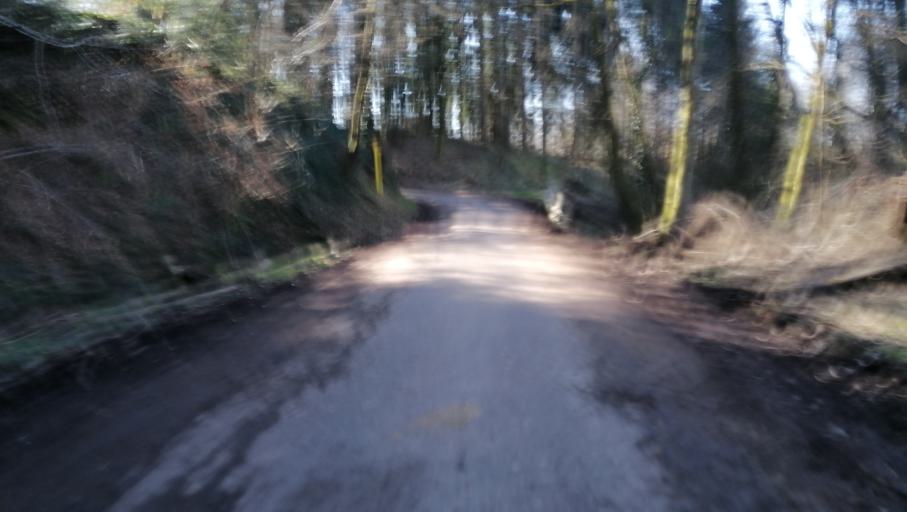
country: CH
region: Aargau
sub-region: Bezirk Rheinfelden
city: Mumpf
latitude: 47.5803
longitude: 7.9189
